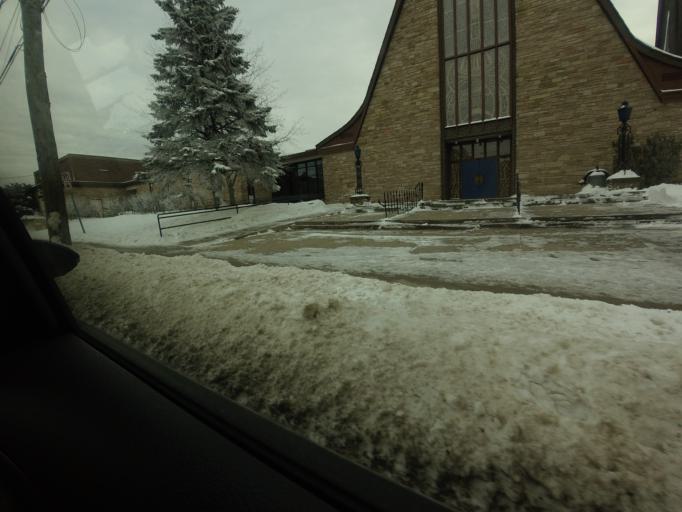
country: CA
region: New Brunswick
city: Fredericton
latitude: 45.9595
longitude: -66.6400
